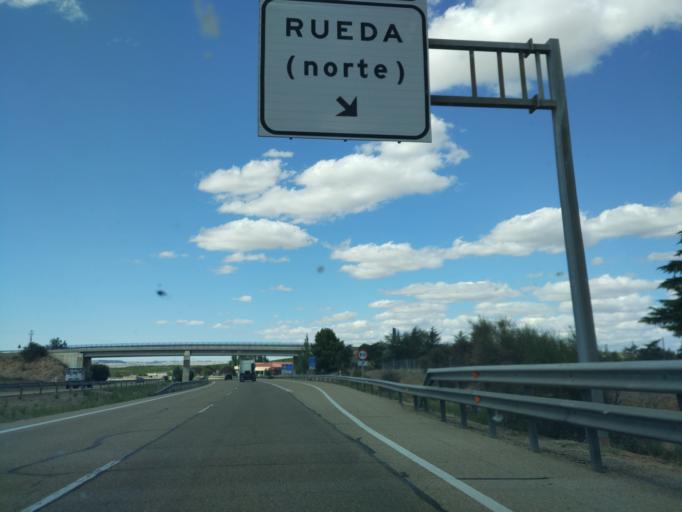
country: ES
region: Castille and Leon
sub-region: Provincia de Valladolid
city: Rueda
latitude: 41.4202
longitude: -4.9651
